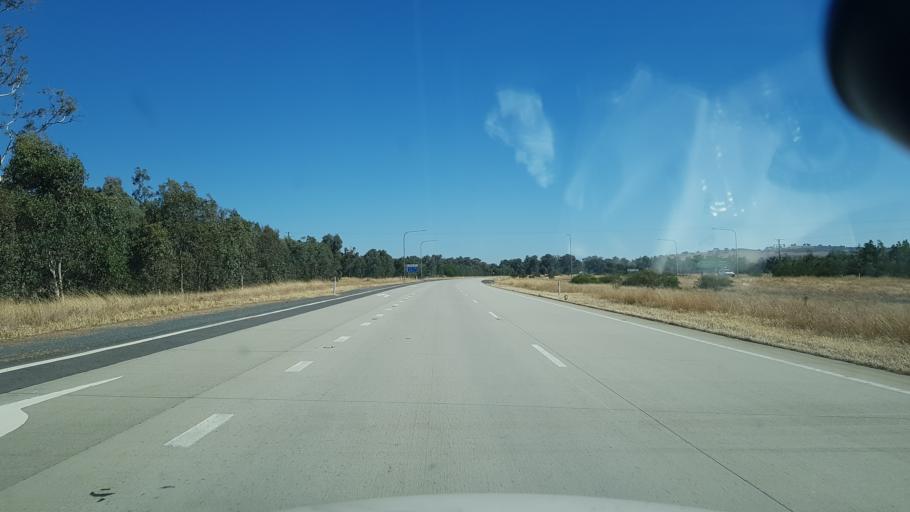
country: AU
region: New South Wales
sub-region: Greater Hume Shire
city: Holbrook
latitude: -35.9104
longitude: 147.1557
